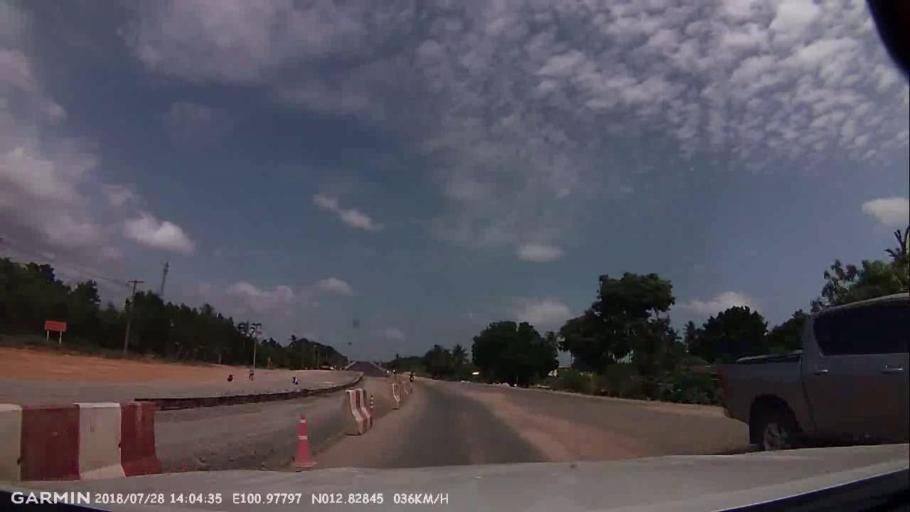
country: TH
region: Rayong
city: Ban Chang
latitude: 12.8283
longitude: 100.9778
